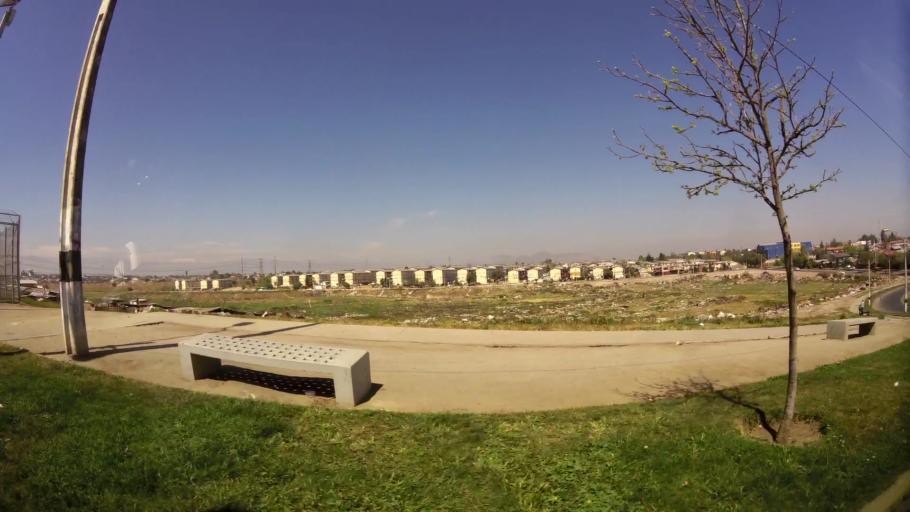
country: CL
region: Santiago Metropolitan
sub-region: Provincia de Santiago
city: Lo Prado
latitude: -33.4903
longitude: -70.7339
